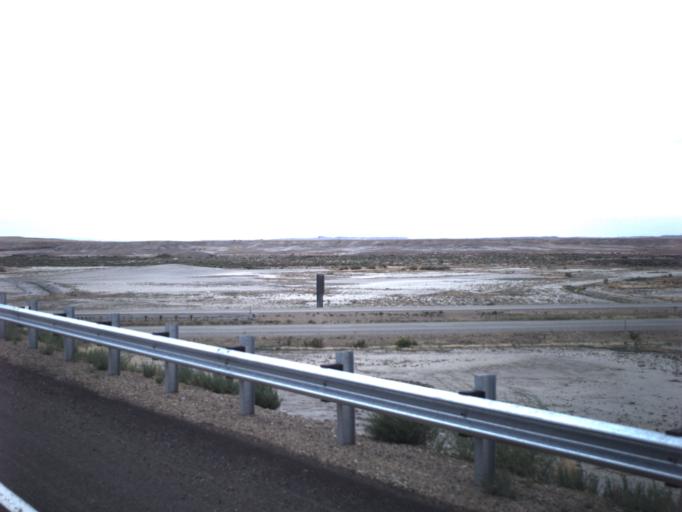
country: US
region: Utah
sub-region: Carbon County
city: East Carbon City
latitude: 38.9822
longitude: -110.2341
